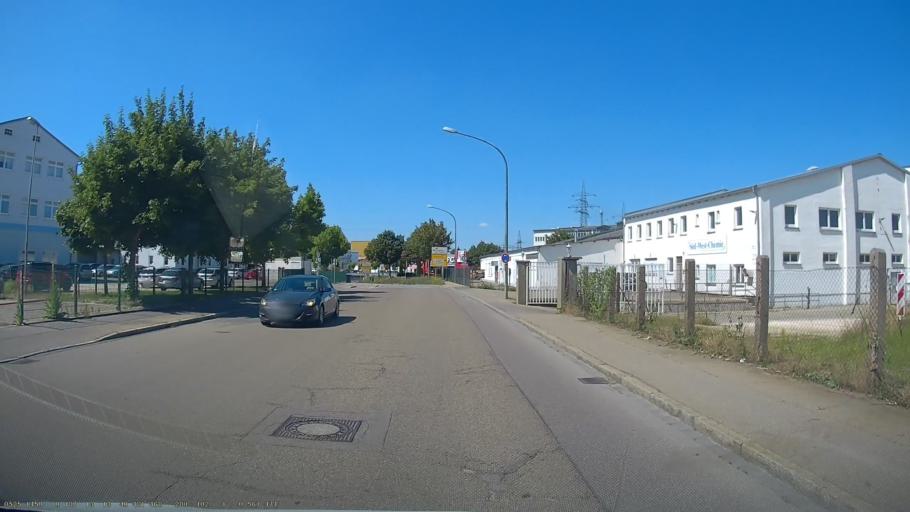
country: DE
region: Bavaria
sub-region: Swabia
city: Neu-Ulm
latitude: 48.3943
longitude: 10.0219
